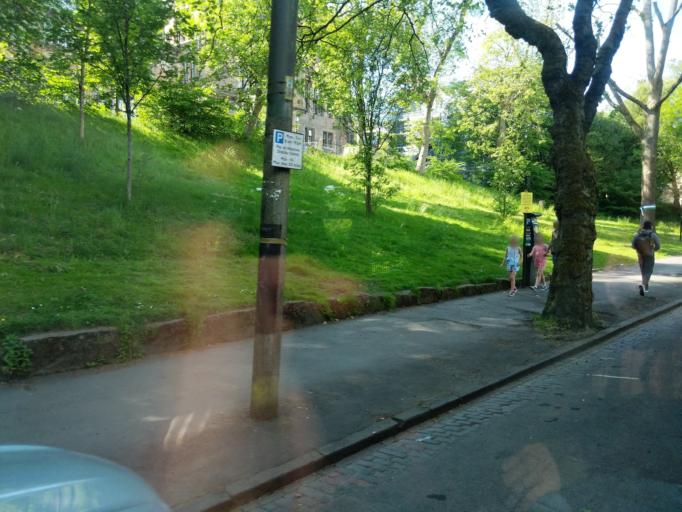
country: GB
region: Scotland
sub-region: Glasgow City
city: Glasgow
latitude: 55.8711
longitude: -4.2857
